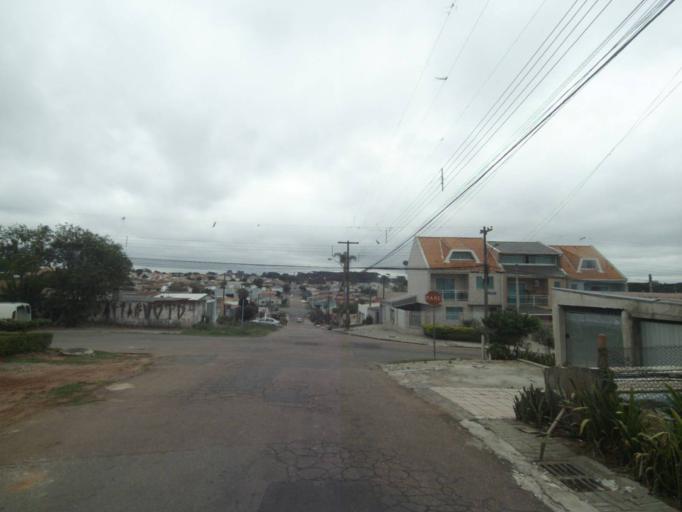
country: BR
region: Parana
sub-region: Sao Jose Dos Pinhais
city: Sao Jose dos Pinhais
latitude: -25.5424
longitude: -49.2911
